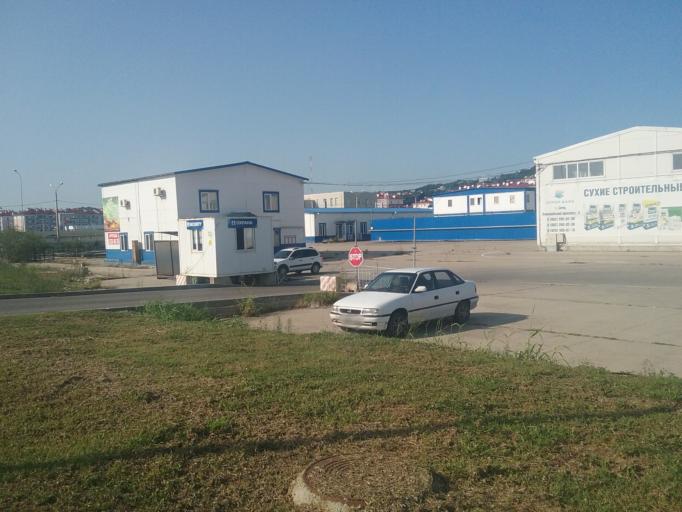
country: RU
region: Krasnodarskiy
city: Vysokoye
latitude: 43.3979
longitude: 39.9845
